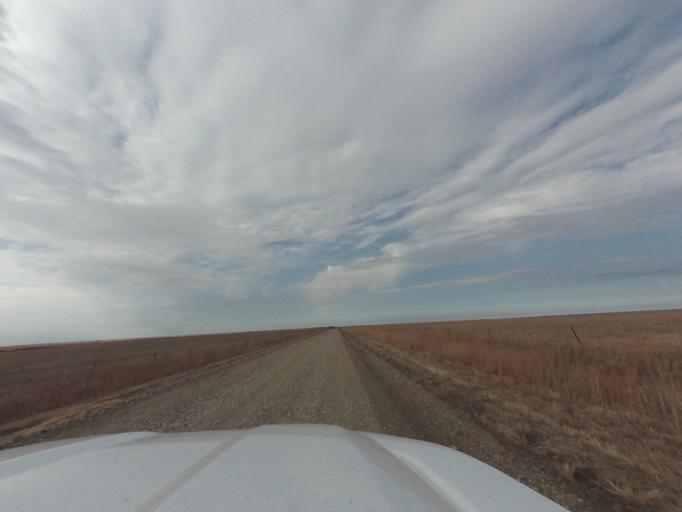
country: US
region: Kansas
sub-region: Chase County
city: Cottonwood Falls
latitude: 38.2171
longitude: -96.7184
